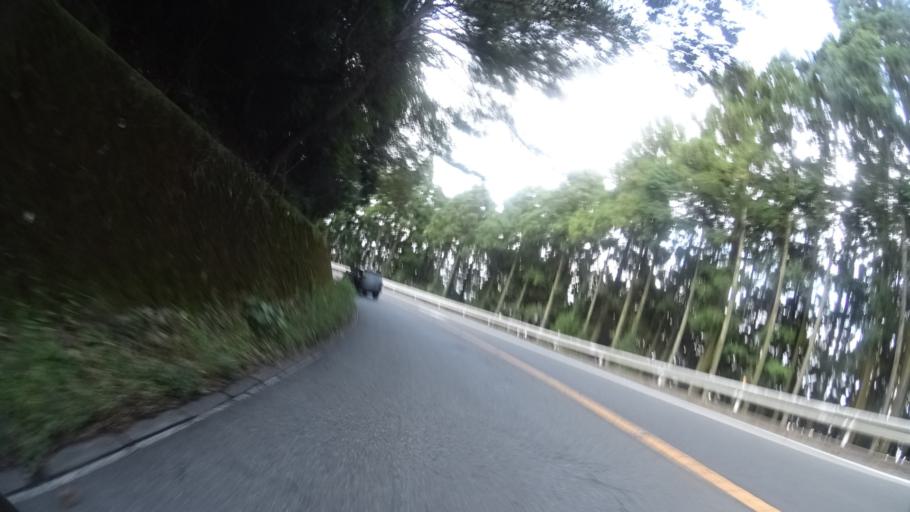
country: JP
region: Oita
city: Beppu
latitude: 33.2872
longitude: 131.4583
